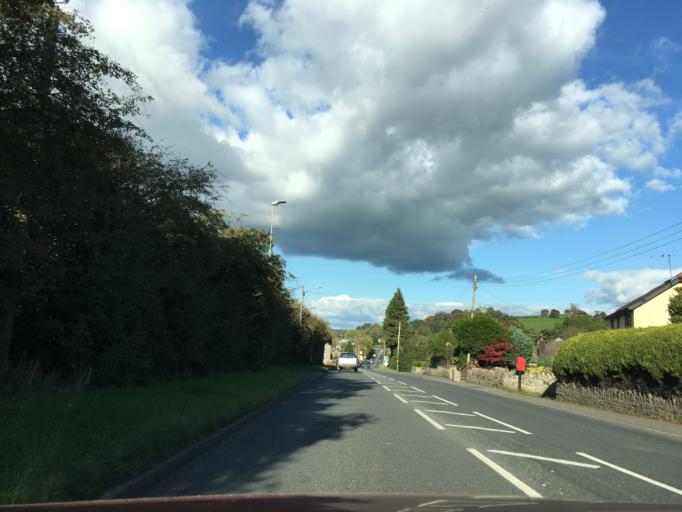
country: GB
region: Wales
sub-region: Sir Powys
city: Hay
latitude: 52.0308
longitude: -3.2075
